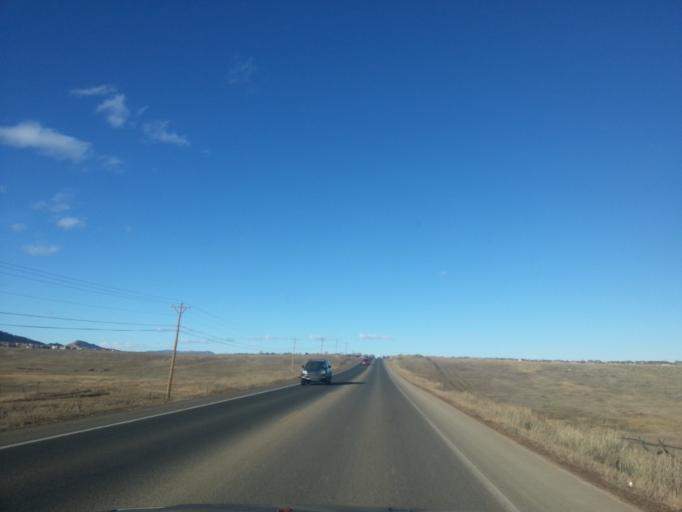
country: US
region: Colorado
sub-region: Larimer County
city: Fort Collins
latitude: 40.5092
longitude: -105.1153
